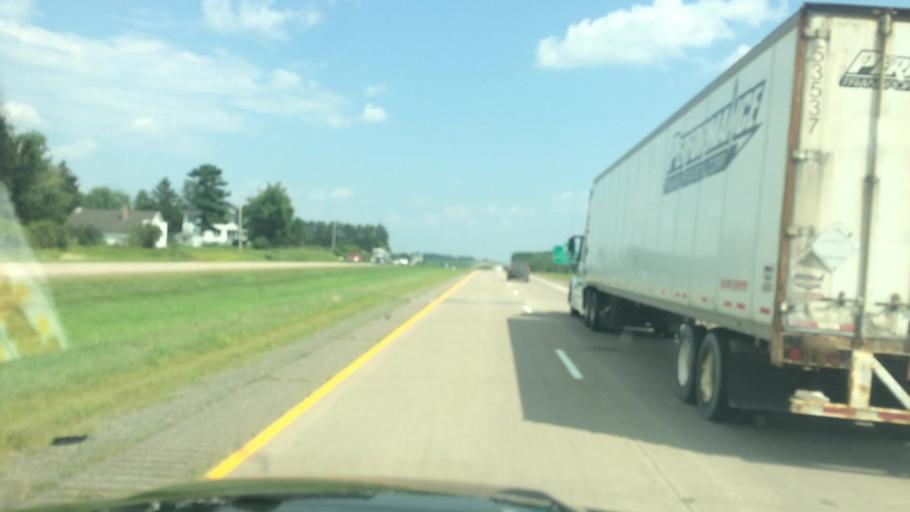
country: US
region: Wisconsin
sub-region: Marathon County
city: Athens
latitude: 44.9454
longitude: -90.1078
